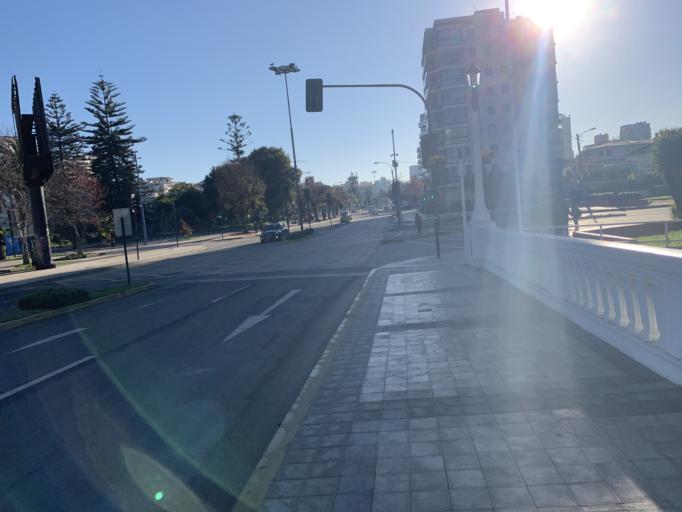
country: CL
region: Valparaiso
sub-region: Provincia de Valparaiso
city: Vina del Mar
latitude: -33.0207
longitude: -71.5604
